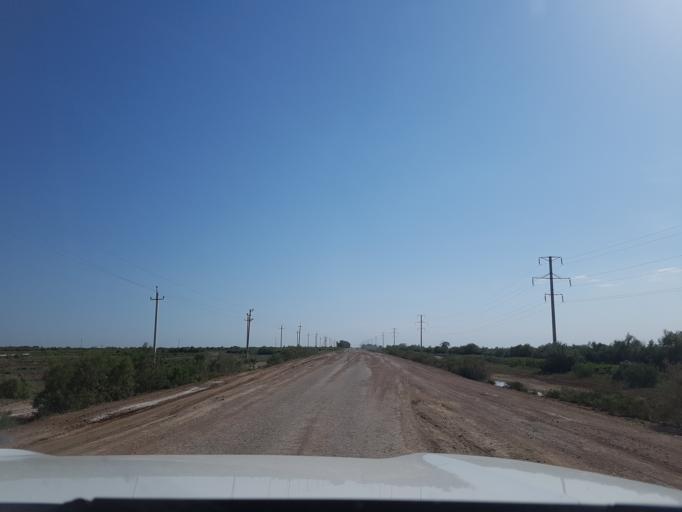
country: TM
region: Dasoguz
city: Koeneuergench
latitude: 42.1230
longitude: 58.9353
